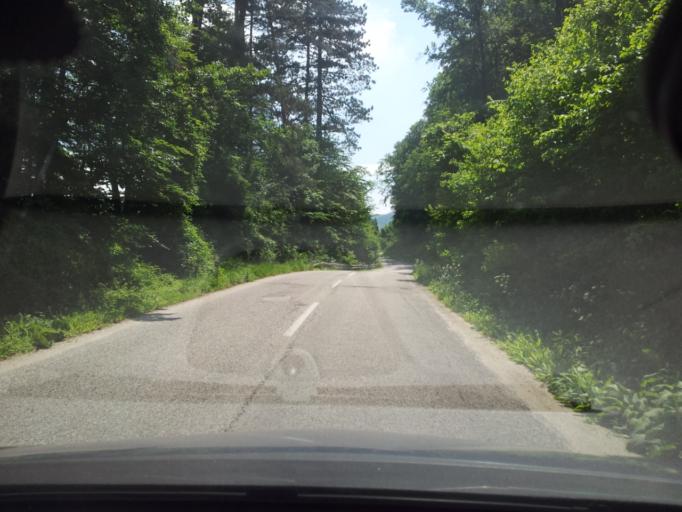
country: SK
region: Nitriansky
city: Partizanske
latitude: 48.5791
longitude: 18.4525
